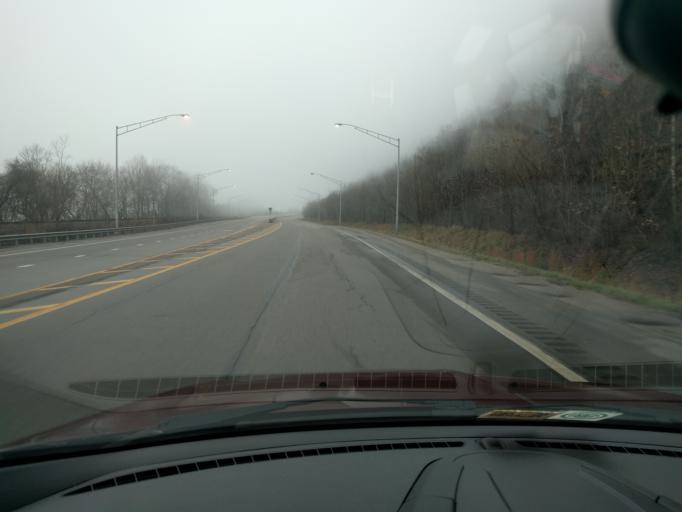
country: US
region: West Virginia
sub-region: Kanawha County
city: Chesapeake
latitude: 38.2022
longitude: -81.4838
